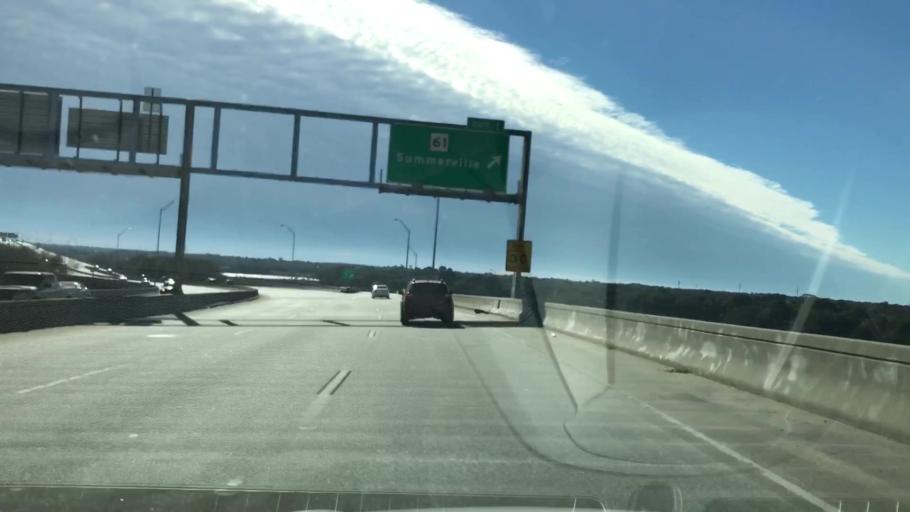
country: US
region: South Carolina
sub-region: Charleston County
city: Charleston
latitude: 32.7789
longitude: -79.9577
